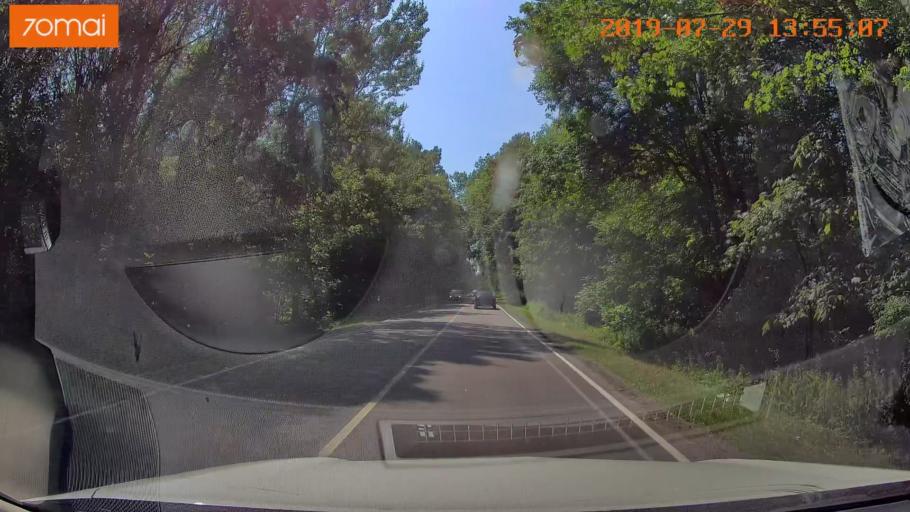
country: RU
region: Kaliningrad
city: Primorsk
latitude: 54.7178
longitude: 19.9600
